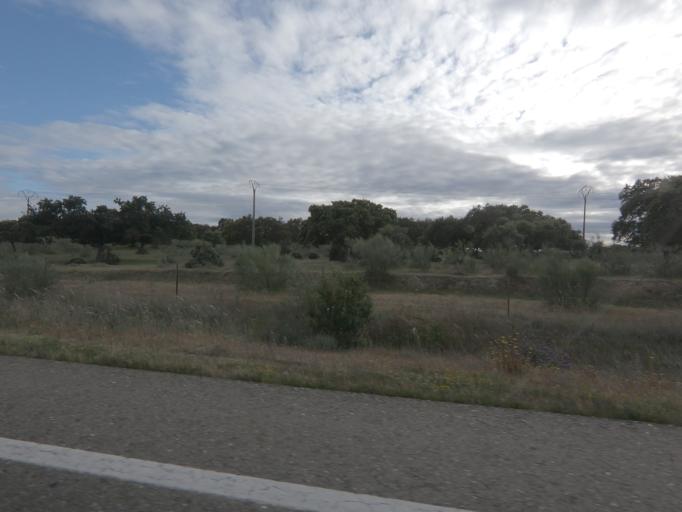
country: ES
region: Extremadura
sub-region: Provincia de Caceres
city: Torrejoncillo
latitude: 39.9181
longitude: -6.4902
